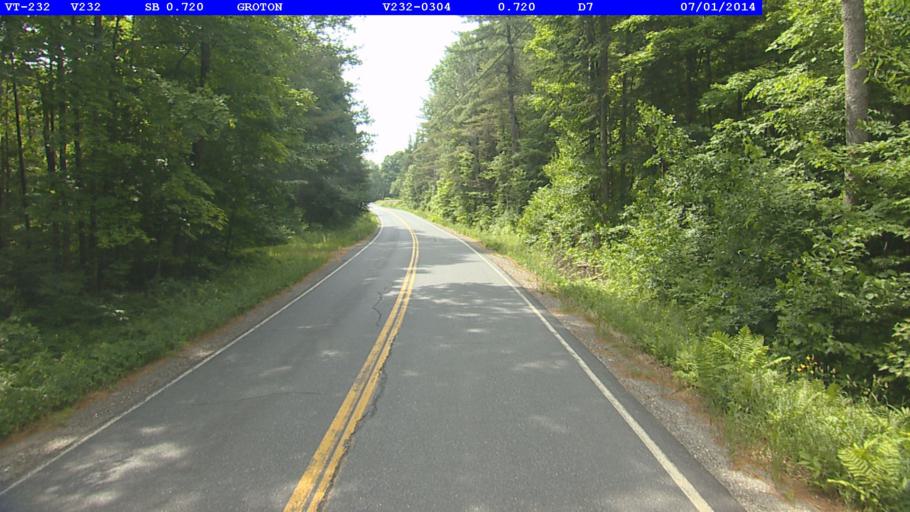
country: US
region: New Hampshire
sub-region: Grafton County
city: Woodsville
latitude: 44.2293
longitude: -72.2298
